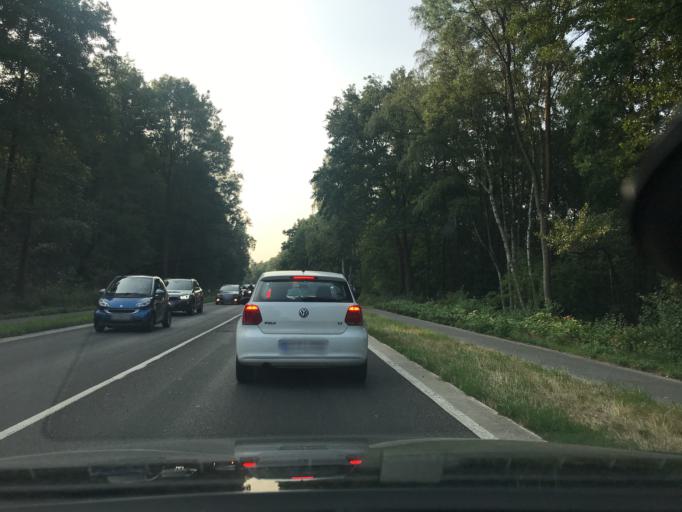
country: DE
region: North Rhine-Westphalia
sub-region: Regierungsbezirk Dusseldorf
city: Erkrath
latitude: 51.2089
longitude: 6.8771
